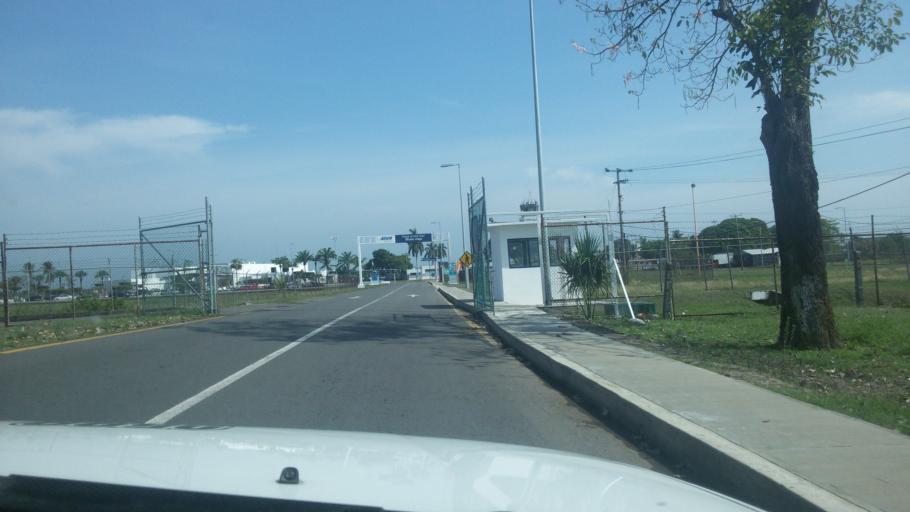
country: MX
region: Chiapas
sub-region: Tapachula
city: Congregacion Reforma
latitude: 14.7886
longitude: -92.3666
